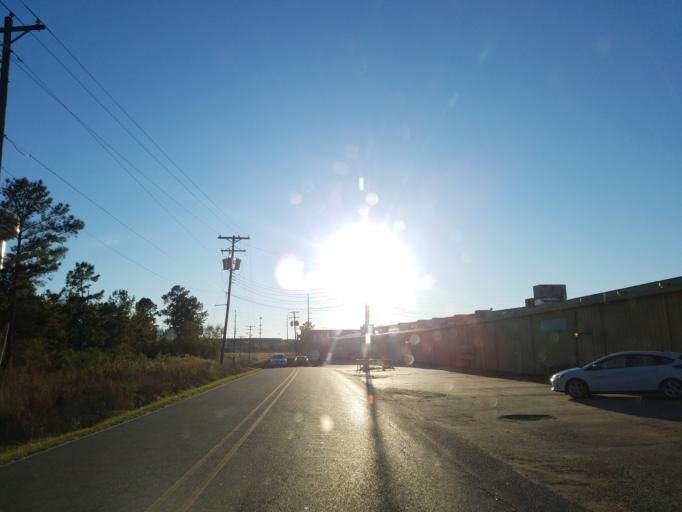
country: US
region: Mississippi
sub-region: Lamar County
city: Arnold Line
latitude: 31.3301
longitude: -89.3715
